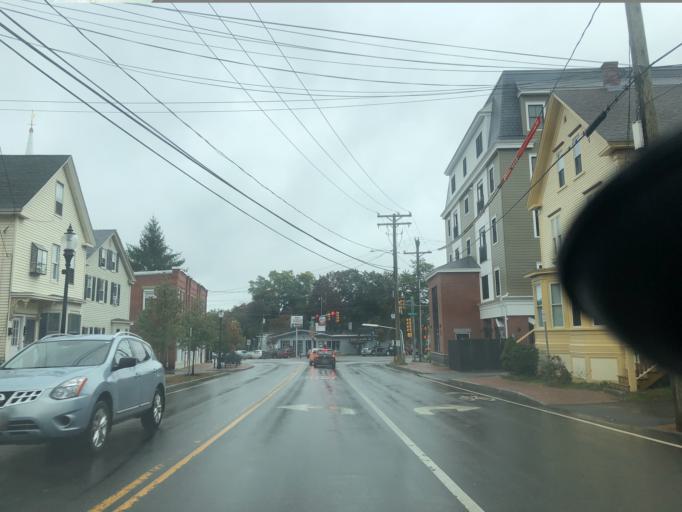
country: US
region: New Hampshire
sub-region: Strafford County
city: Dover
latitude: 43.1905
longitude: -70.8749
